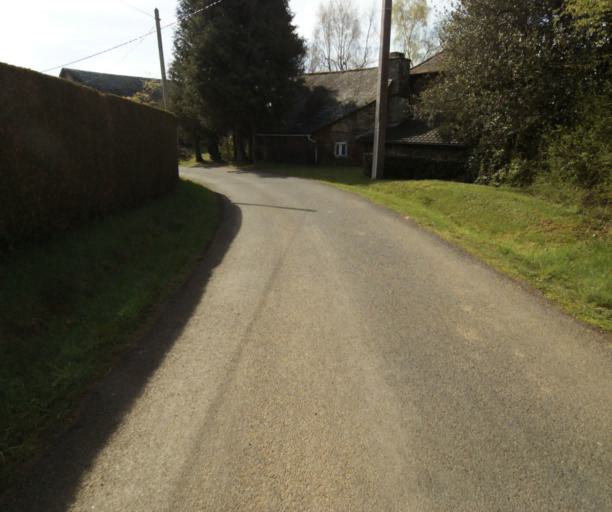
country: FR
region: Limousin
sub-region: Departement de la Correze
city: Laguenne
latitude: 45.2708
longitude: 1.8140
